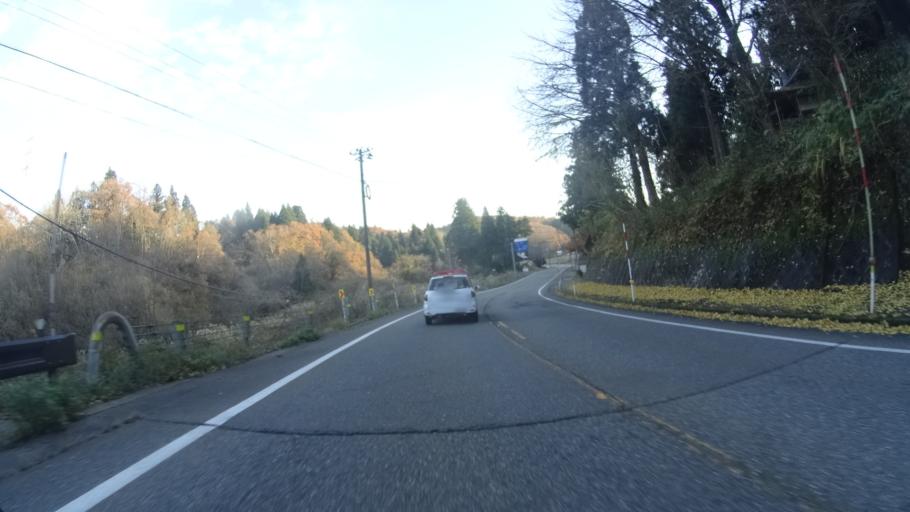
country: JP
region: Niigata
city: Kashiwazaki
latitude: 37.4096
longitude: 138.6860
